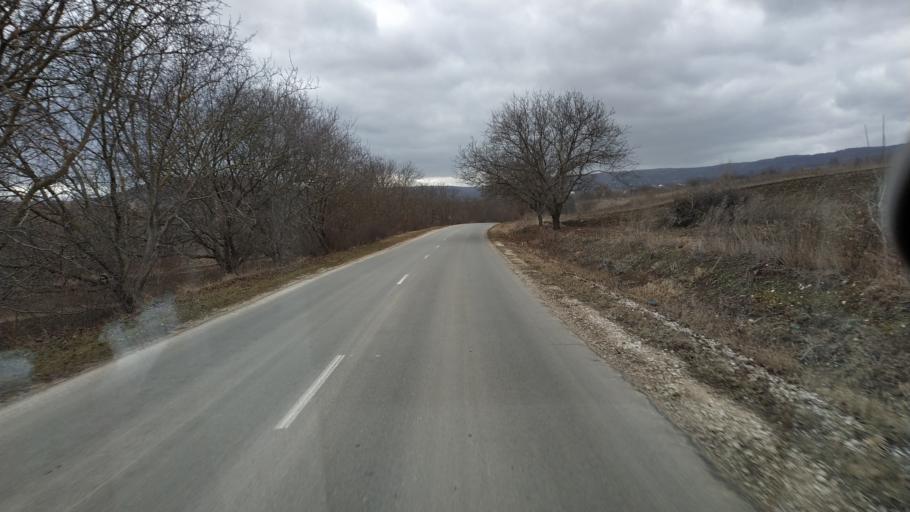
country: MD
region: Calarasi
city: Calarasi
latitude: 47.2406
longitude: 28.1629
